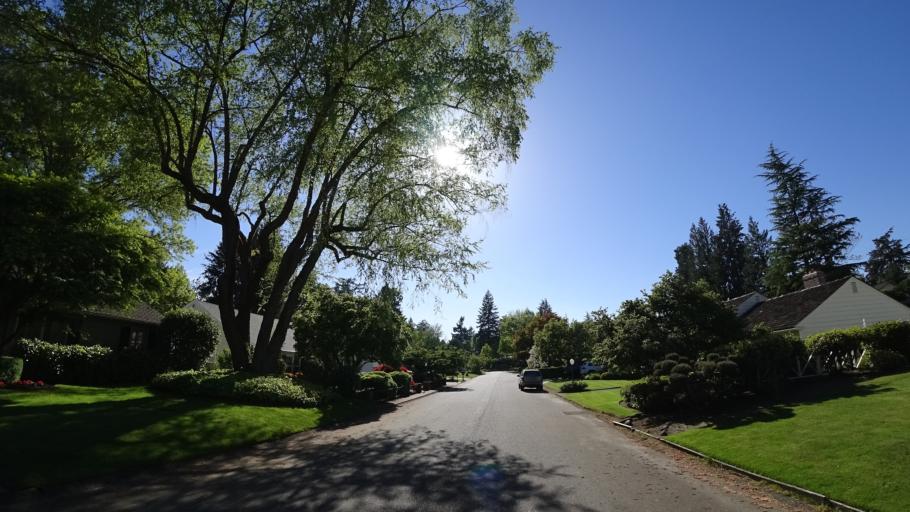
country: US
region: Oregon
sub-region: Washington County
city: West Slope
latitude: 45.4918
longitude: -122.7561
